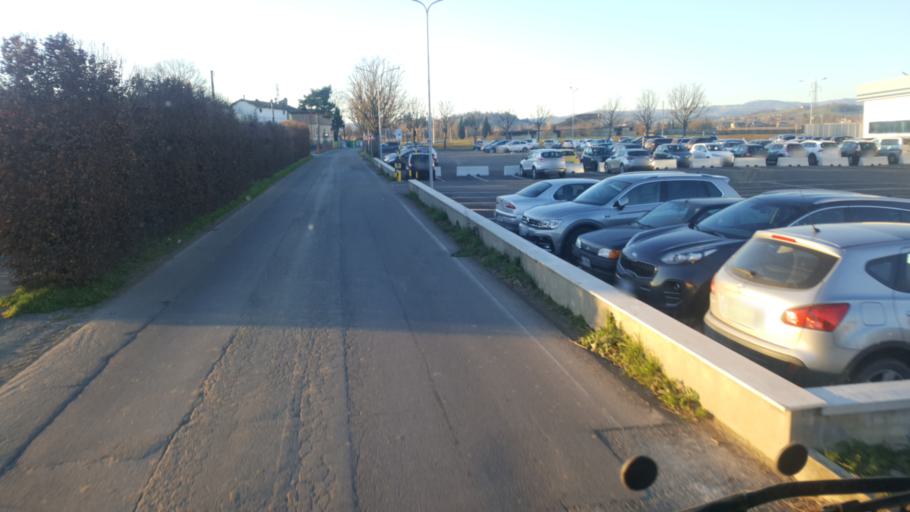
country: IT
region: Emilia-Romagna
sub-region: Provincia di Modena
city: Ca' di Sola
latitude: 44.5367
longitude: 10.9690
